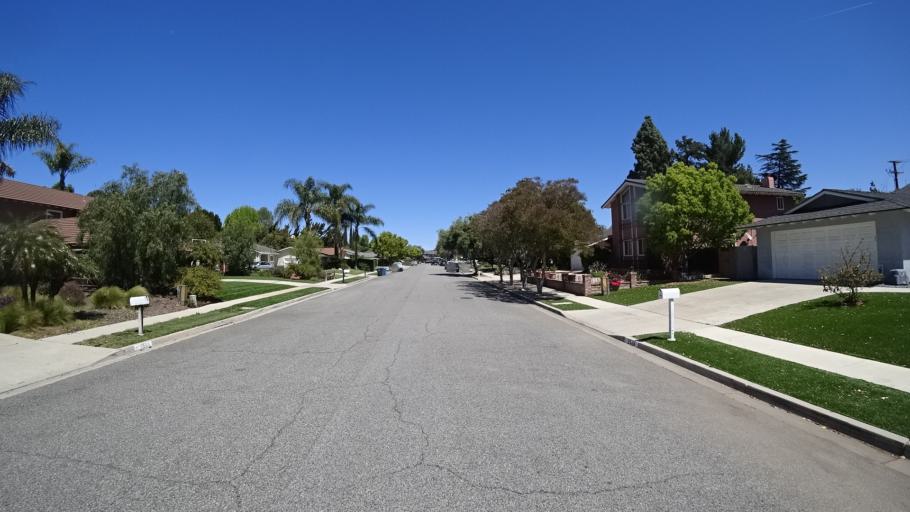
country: US
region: California
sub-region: Ventura County
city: Thousand Oaks
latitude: 34.1985
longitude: -118.8431
